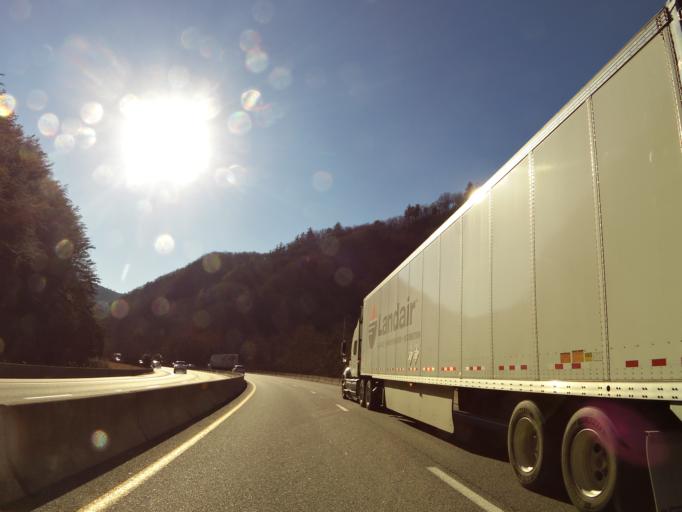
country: US
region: North Carolina
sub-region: Haywood County
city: Cove Creek
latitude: 35.7673
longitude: -83.0804
